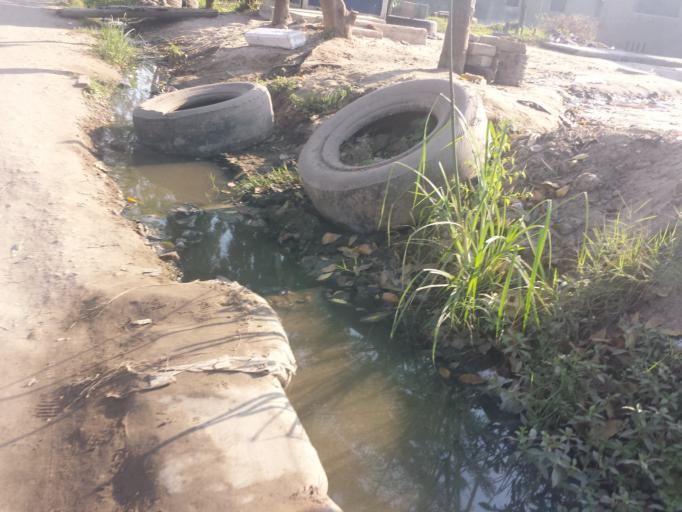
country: TZ
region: Dar es Salaam
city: Magomeni
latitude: -6.8326
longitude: 39.2213
